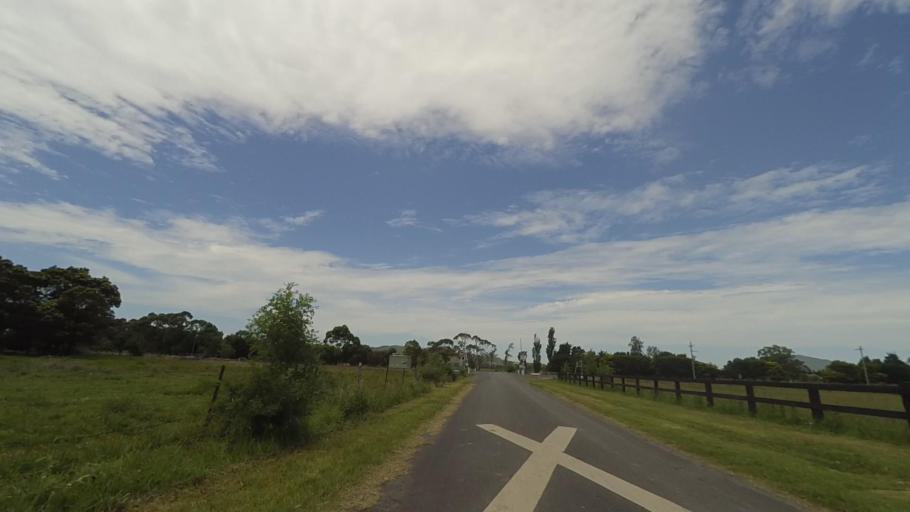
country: AU
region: New South Wales
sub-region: Shoalhaven Shire
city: Berry
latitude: -34.7897
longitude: 150.6786
